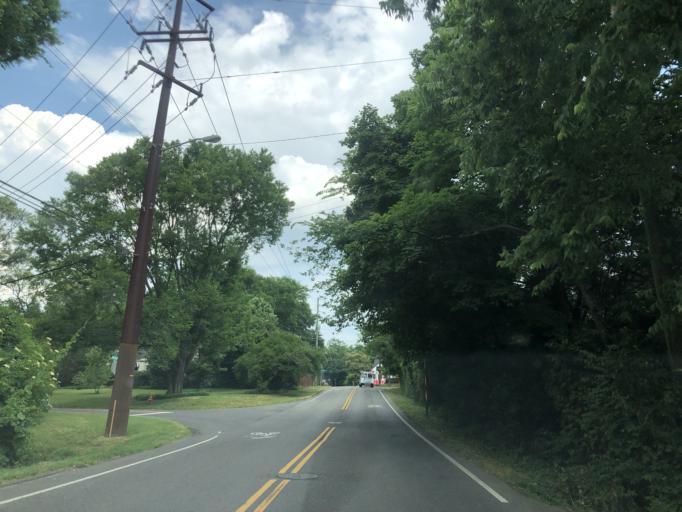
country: US
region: Tennessee
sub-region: Davidson County
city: Belle Meade
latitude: 36.1233
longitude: -86.8199
